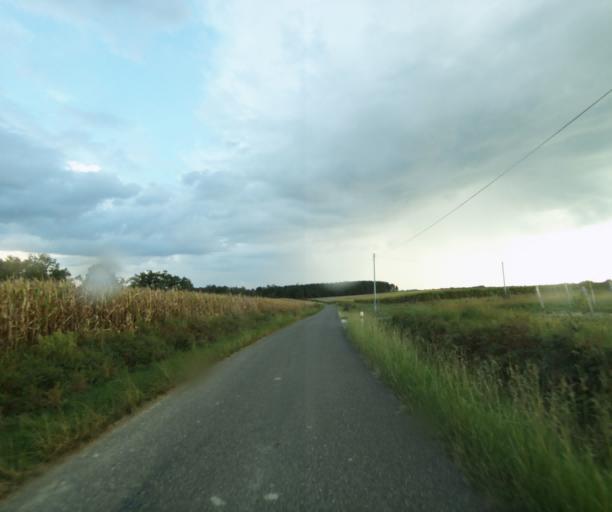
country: FR
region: Midi-Pyrenees
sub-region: Departement du Gers
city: Cazaubon
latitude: 43.9102
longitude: -0.0919
